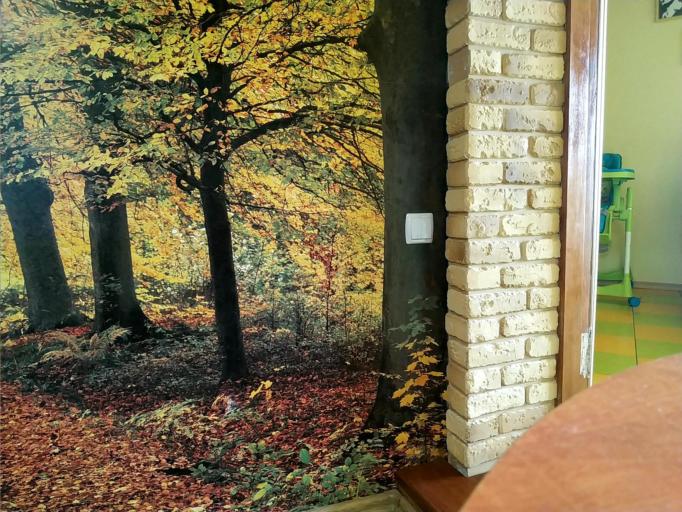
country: RU
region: Smolensk
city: Ozernyy
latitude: 55.4435
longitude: 32.6677
